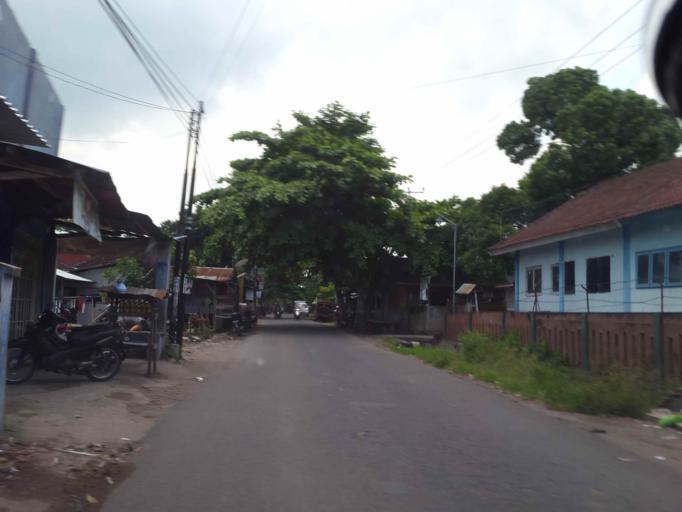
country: ID
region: West Nusa Tenggara
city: Kekeri
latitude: -8.5534
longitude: 116.0932
